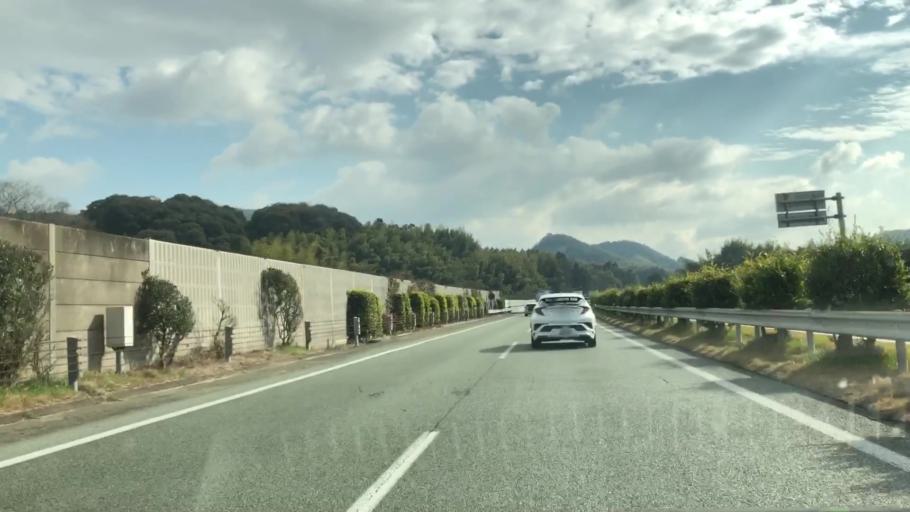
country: JP
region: Fukuoka
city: Setakamachi-takayanagi
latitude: 33.1135
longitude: 130.5300
